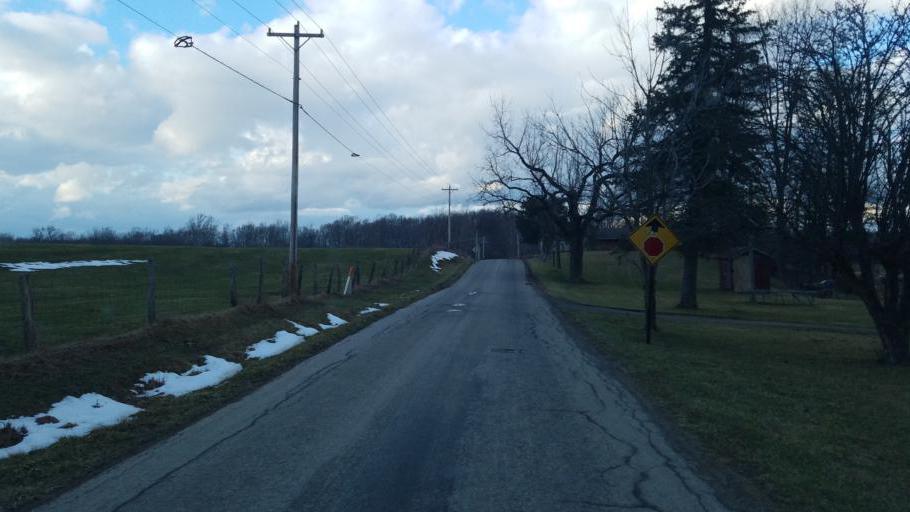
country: US
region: Ohio
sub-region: Richland County
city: Lexington
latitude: 40.6179
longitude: -82.6061
